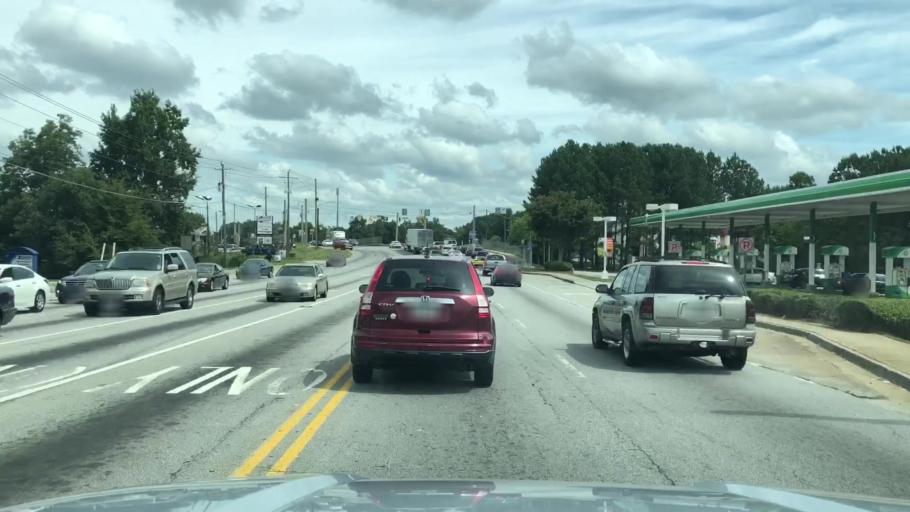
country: US
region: Georgia
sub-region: DeKalb County
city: Redan
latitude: 33.7013
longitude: -84.1716
